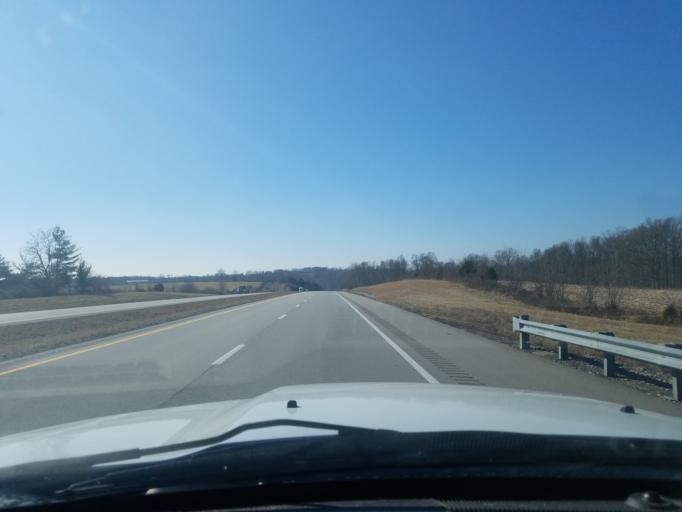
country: US
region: Kentucky
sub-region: Grayson County
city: Leitchfield
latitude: 37.4573
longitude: -86.3128
